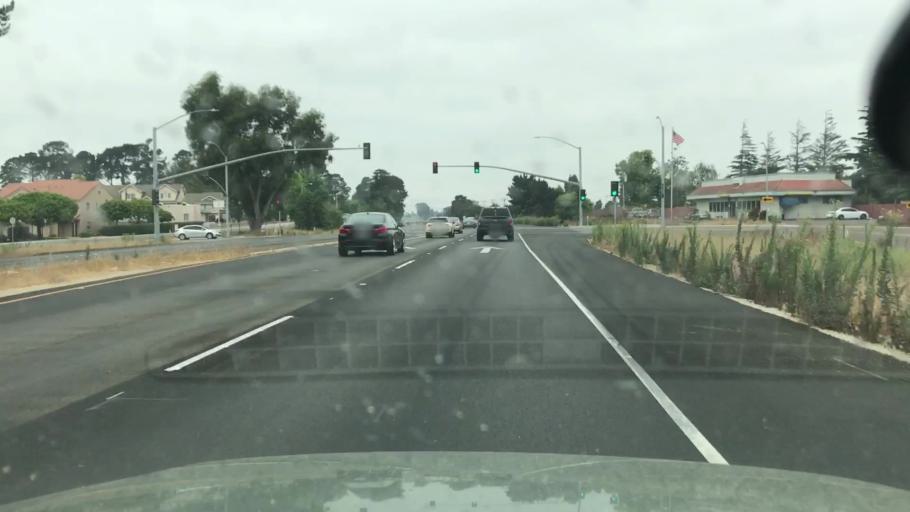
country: US
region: California
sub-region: Santa Barbara County
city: Orcutt
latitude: 34.8985
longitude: -120.4361
